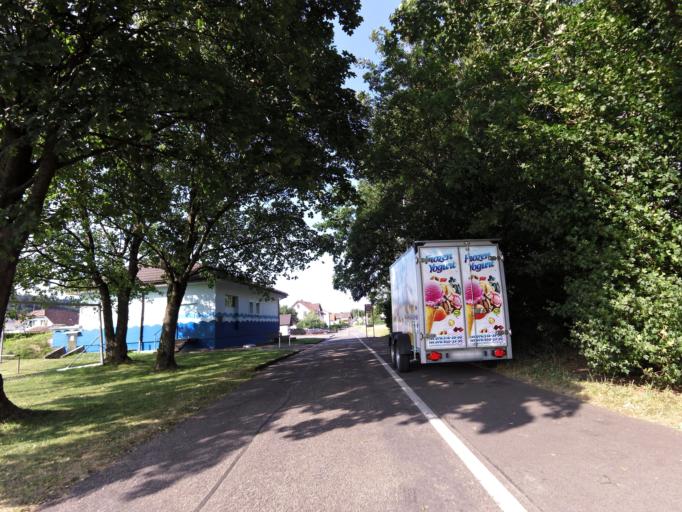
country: CH
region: Solothurn
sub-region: Bezirk Olten
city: Niedergosgen
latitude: 47.3667
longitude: 7.9917
